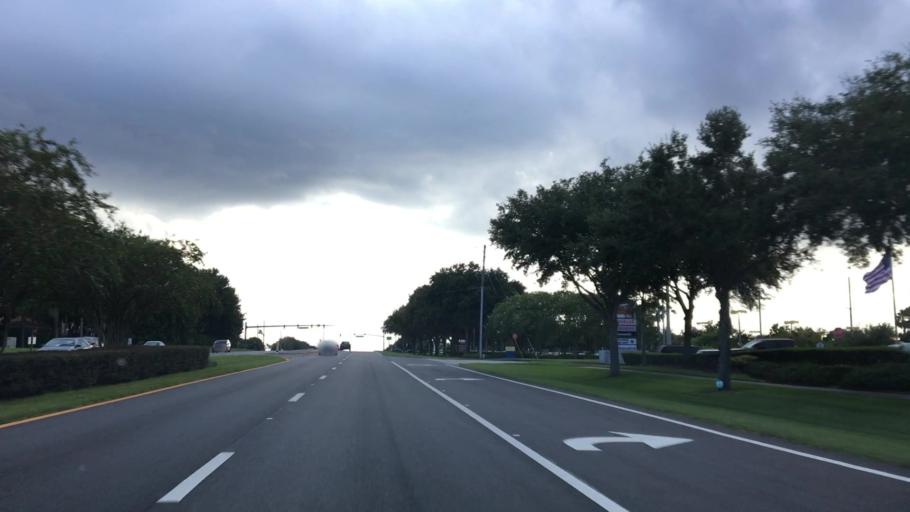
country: US
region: Florida
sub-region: Seminole County
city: Lake Mary
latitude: 28.7944
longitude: -81.3367
